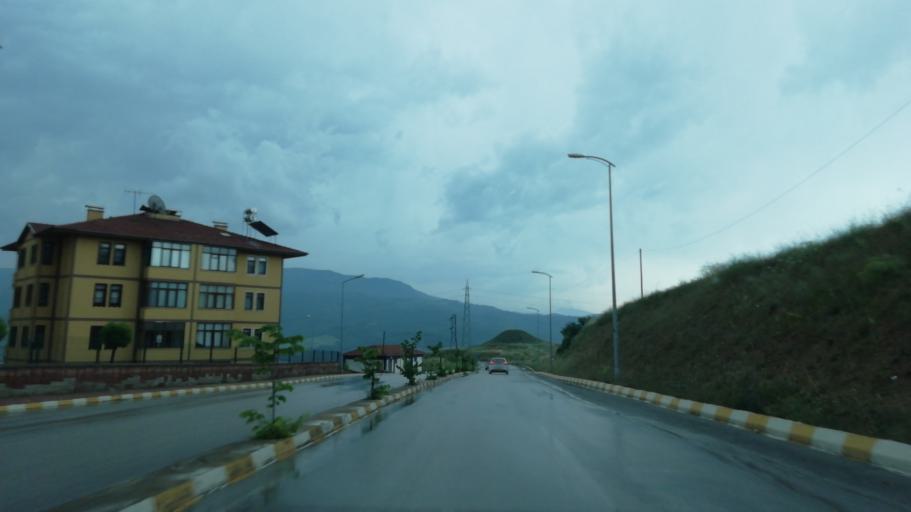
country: TR
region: Karabuk
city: Safranbolu
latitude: 41.2378
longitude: 32.6827
